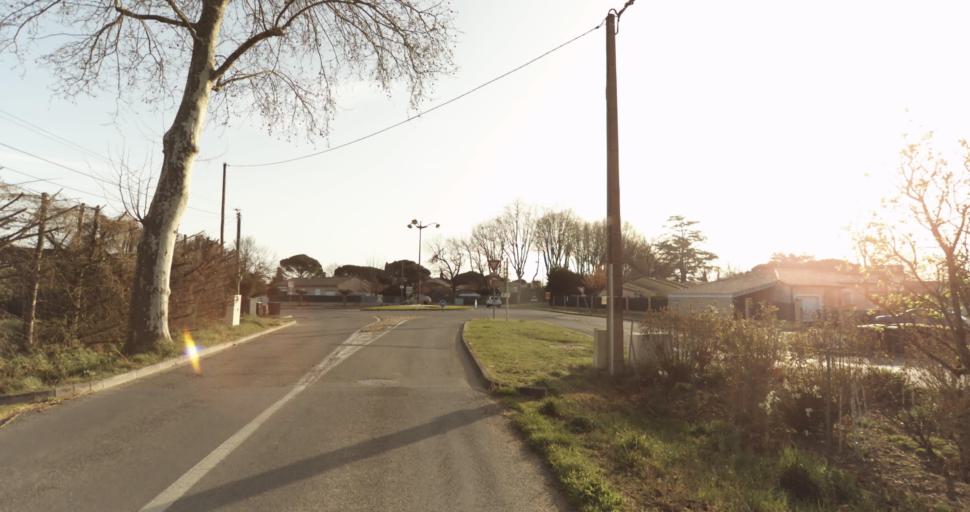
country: FR
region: Midi-Pyrenees
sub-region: Departement du Tarn
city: Saint-Sulpice-la-Pointe
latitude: 43.7769
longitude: 1.6710
